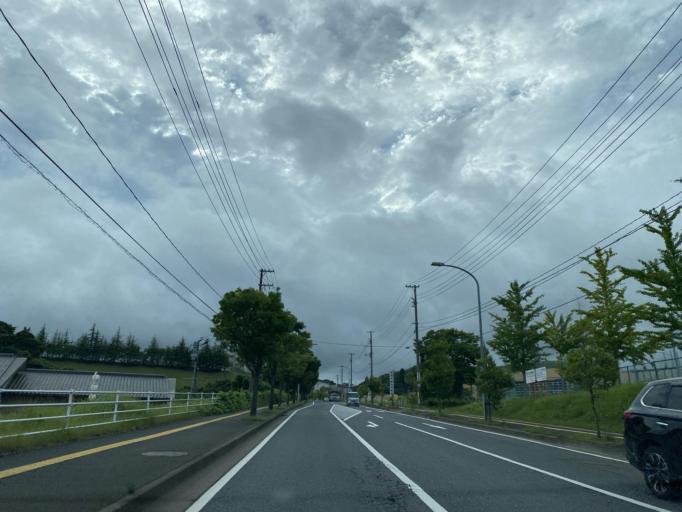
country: JP
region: Miyagi
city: Rifu
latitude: 38.3344
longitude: 140.9697
